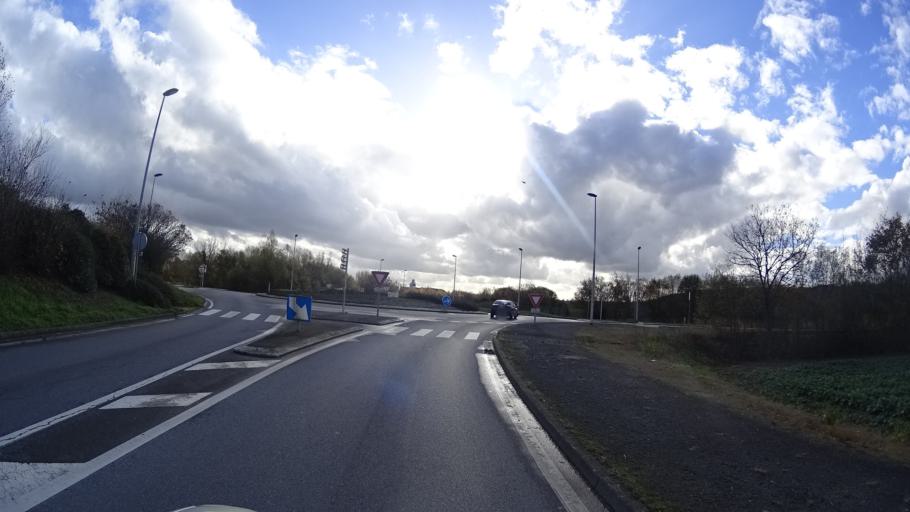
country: FR
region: Brittany
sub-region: Departement d'Ille-et-Vilaine
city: Redon
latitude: 47.6487
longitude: -2.0981
